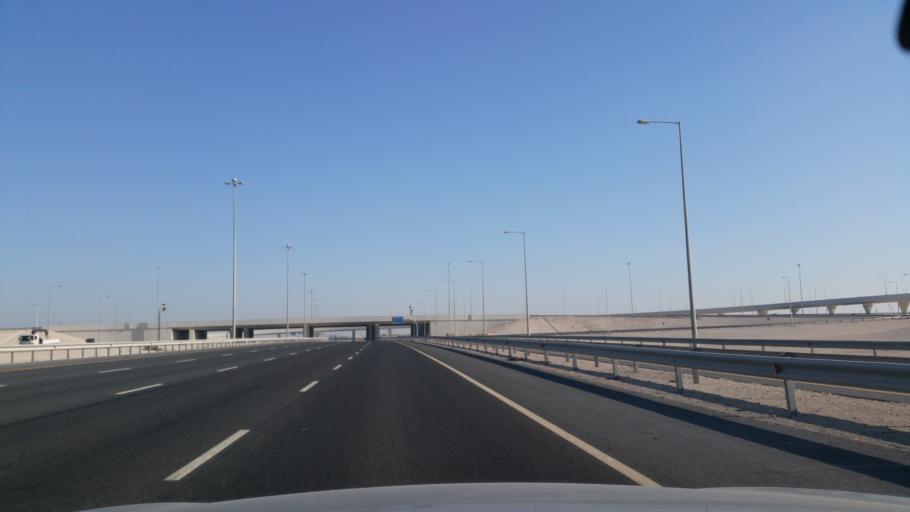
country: QA
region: Al Wakrah
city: Al Wukayr
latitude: 25.1252
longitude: 51.4845
